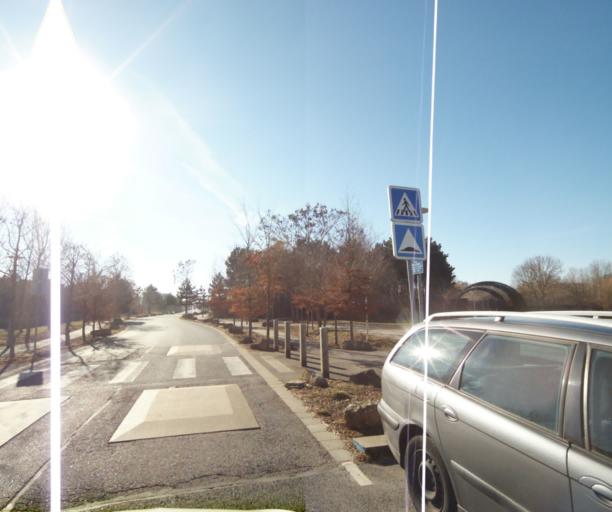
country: FR
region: Lorraine
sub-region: Departement de Meurthe-et-Moselle
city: Maxeville
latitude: 48.7058
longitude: 6.1492
